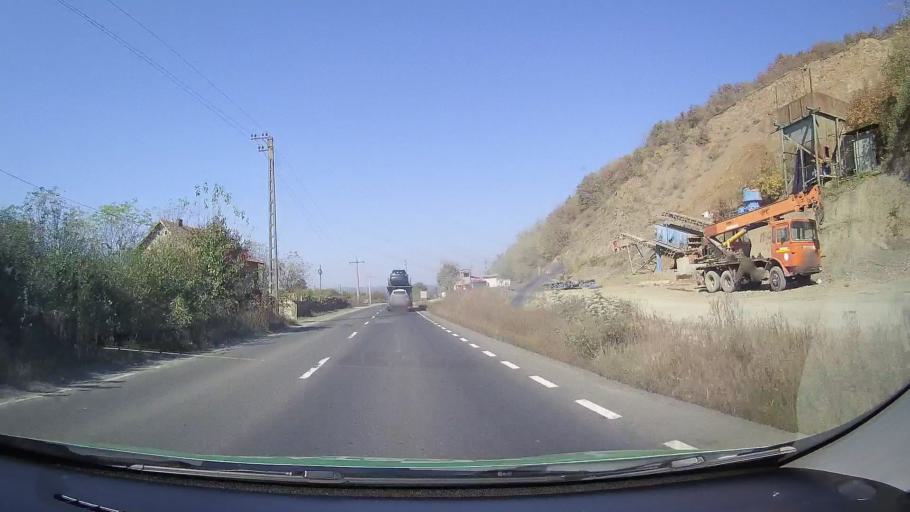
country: RO
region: Arad
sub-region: Comuna Bata
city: Bata
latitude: 46.0560
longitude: 22.0467
